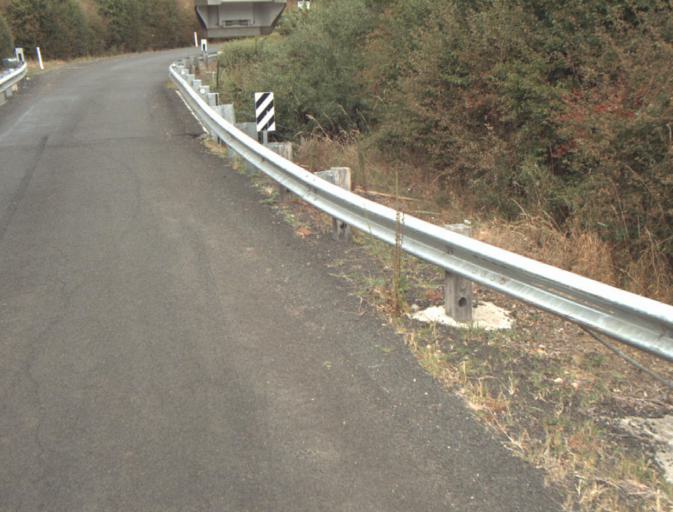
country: AU
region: Tasmania
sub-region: Northern Midlands
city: Evandale
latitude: -41.5305
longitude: 147.2437
